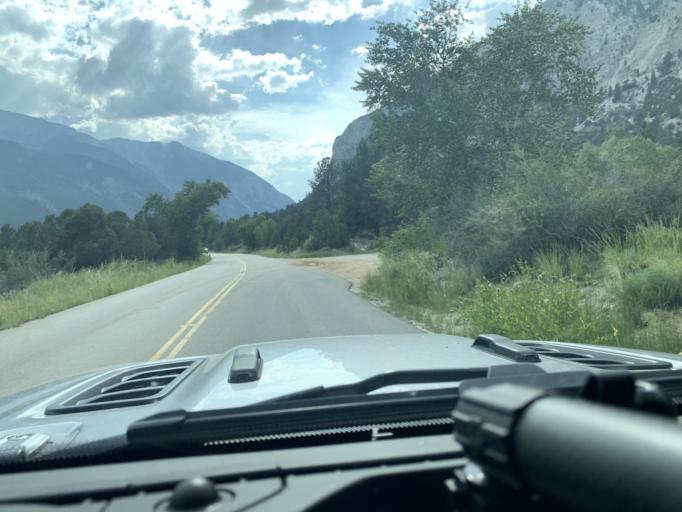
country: US
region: Colorado
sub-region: Chaffee County
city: Buena Vista
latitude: 38.7216
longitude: -106.1873
